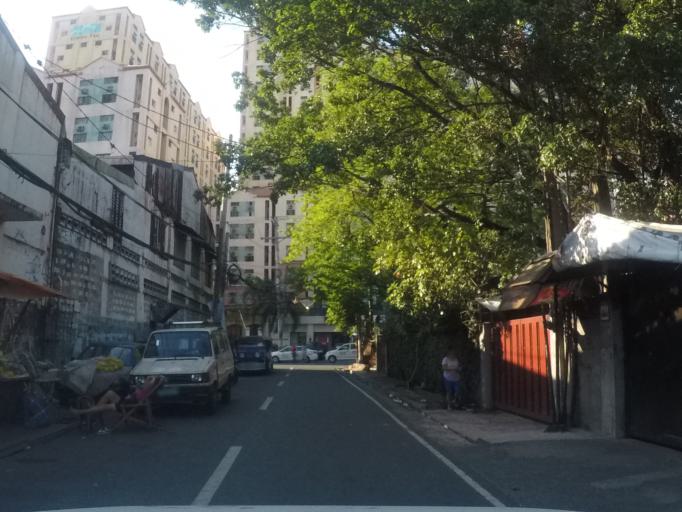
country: PH
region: Metro Manila
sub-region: San Juan
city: San Juan
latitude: 14.6089
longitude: 121.0485
